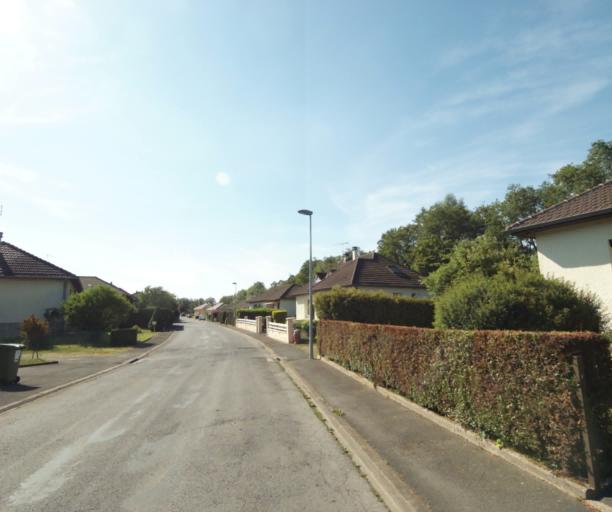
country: FR
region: Champagne-Ardenne
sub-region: Departement des Ardennes
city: Warcq
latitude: 49.7820
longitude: 4.6978
